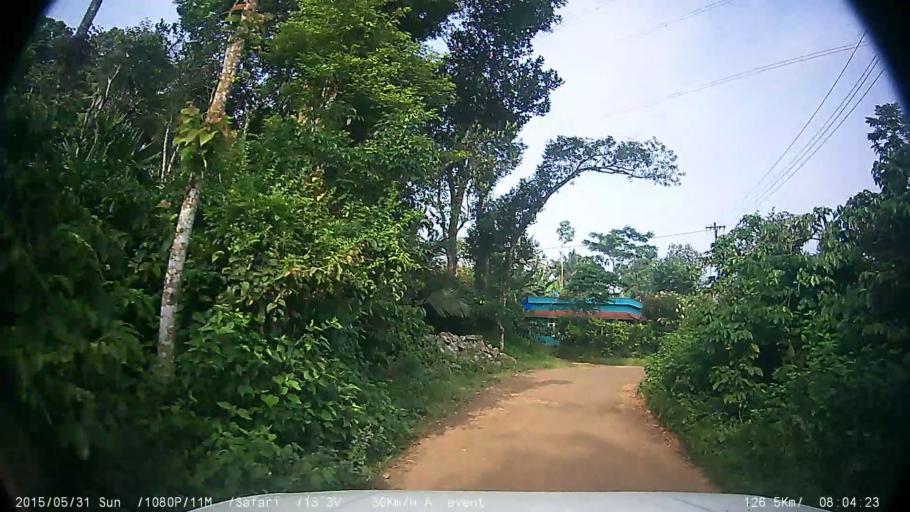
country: IN
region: Kerala
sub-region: Wayanad
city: Kalpetta
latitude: 11.6361
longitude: 76.0395
